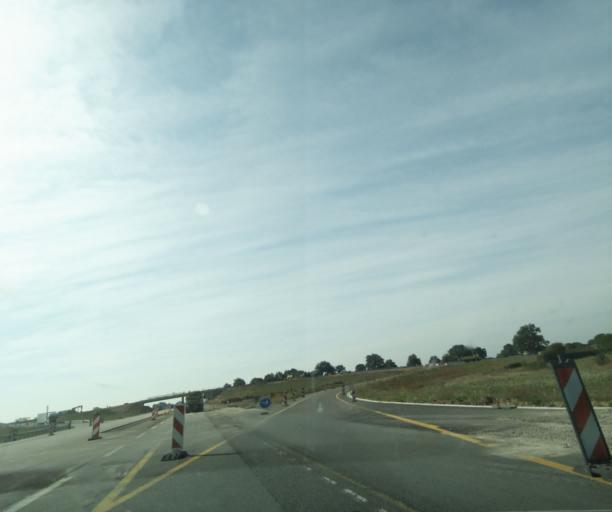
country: FR
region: Bourgogne
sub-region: Departement de Saone-et-Loire
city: Palinges
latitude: 46.5169
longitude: 4.1632
